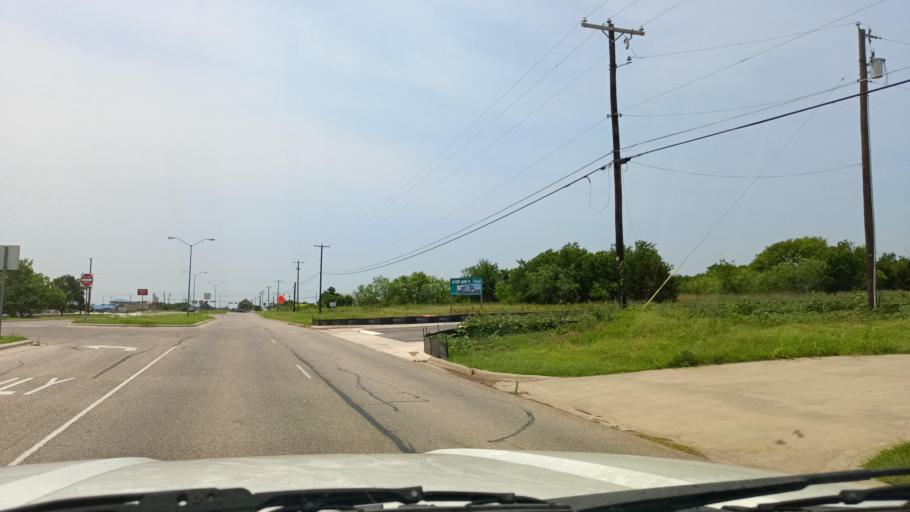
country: US
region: Texas
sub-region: Bell County
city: Morgans Point Resort
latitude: 31.1213
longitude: -97.4149
